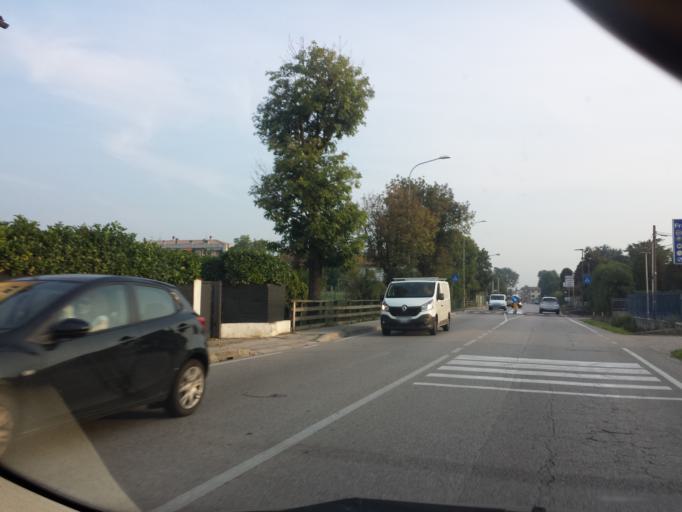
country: IT
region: Veneto
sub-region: Provincia di Vicenza
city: Monticello Conte Otto
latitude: 45.5859
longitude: 11.5559
